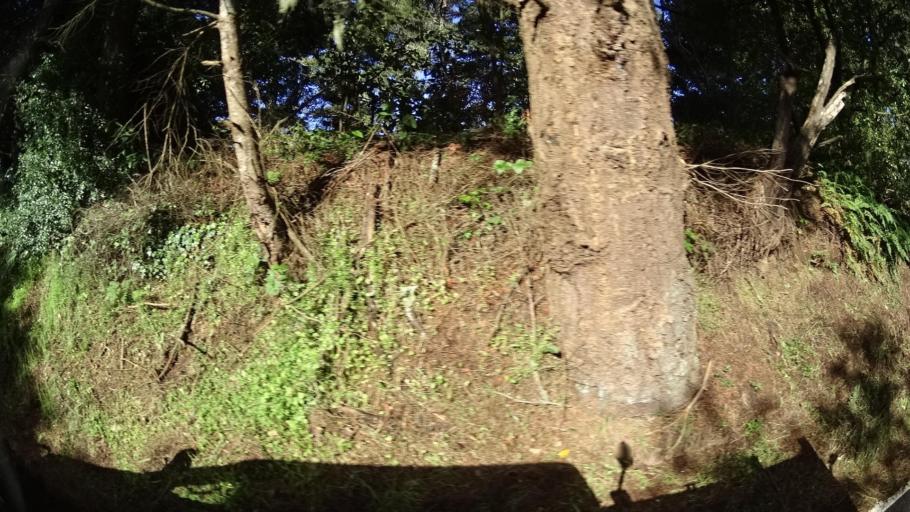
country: US
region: California
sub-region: Humboldt County
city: Westhaven-Moonstone
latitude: 41.0575
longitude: -124.1375
